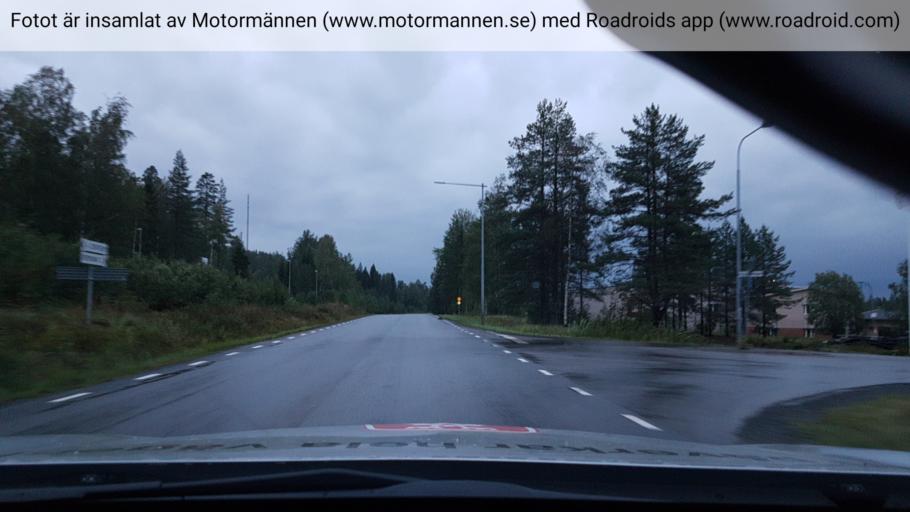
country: SE
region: Vaesterbotten
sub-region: Umea Kommun
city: Ersmark
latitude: 63.8634
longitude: 20.3005
